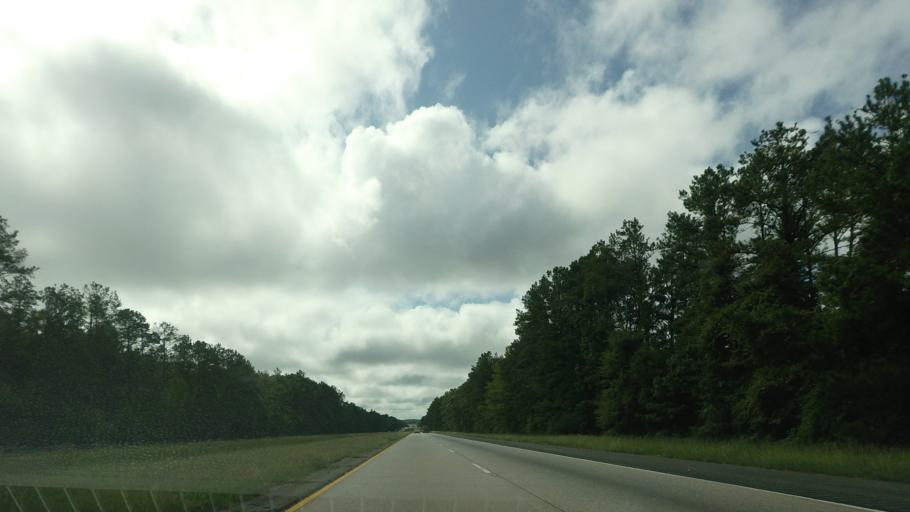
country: US
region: Georgia
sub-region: Bibb County
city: Macon
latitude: 32.7436
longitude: -83.5455
